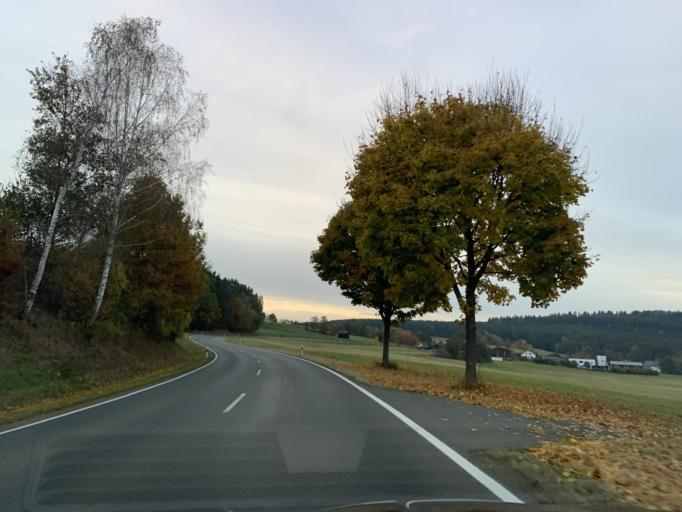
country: DE
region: Bavaria
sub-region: Upper Palatinate
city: Neunburg vorm Wald
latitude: 49.3722
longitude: 12.3786
